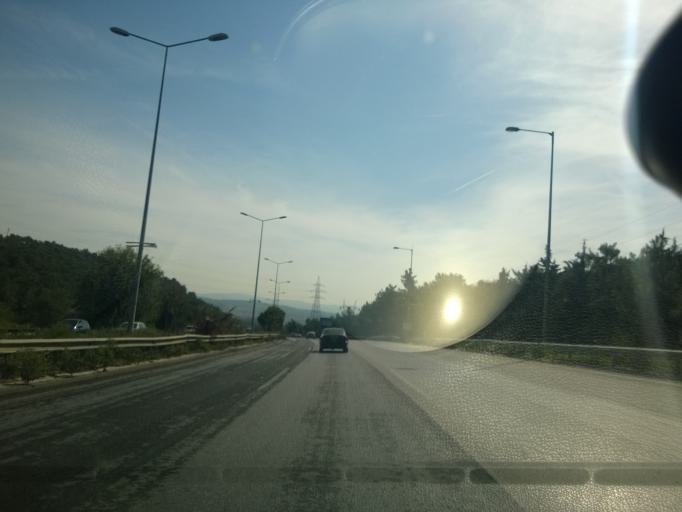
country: GR
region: Central Macedonia
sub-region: Nomos Thessalonikis
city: Agios Pavlos
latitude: 40.6395
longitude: 22.9701
